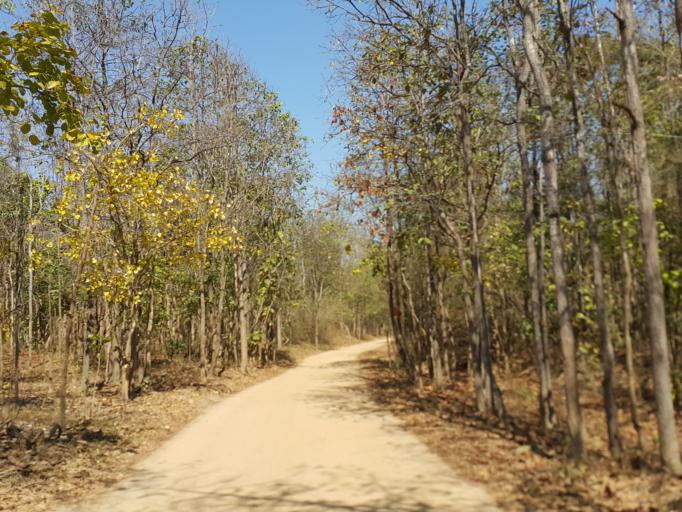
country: TH
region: Chiang Mai
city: Doi Lo
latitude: 18.5273
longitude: 98.7449
